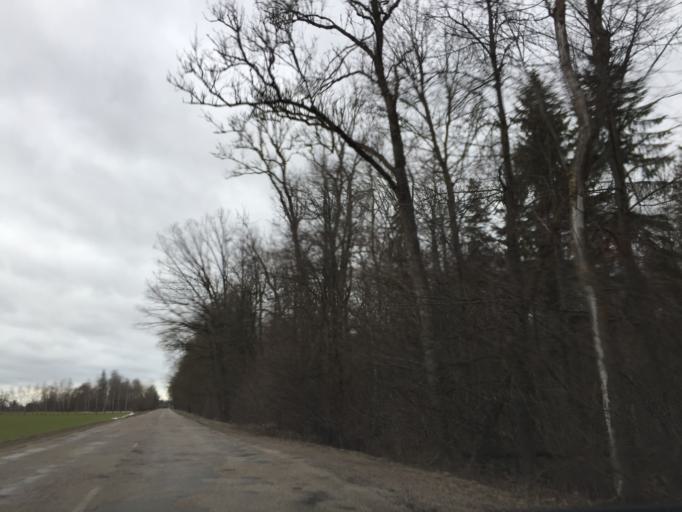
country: LV
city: Tervete
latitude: 56.5363
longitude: 23.5279
